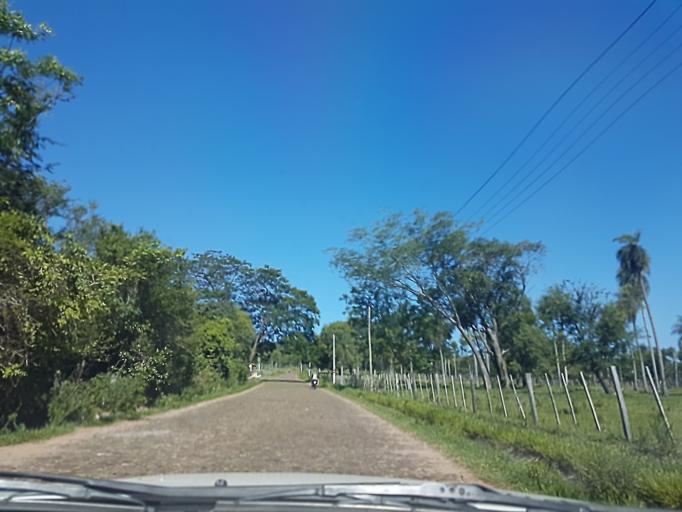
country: PY
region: Cordillera
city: Atyra
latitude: -25.2793
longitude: -57.1607
